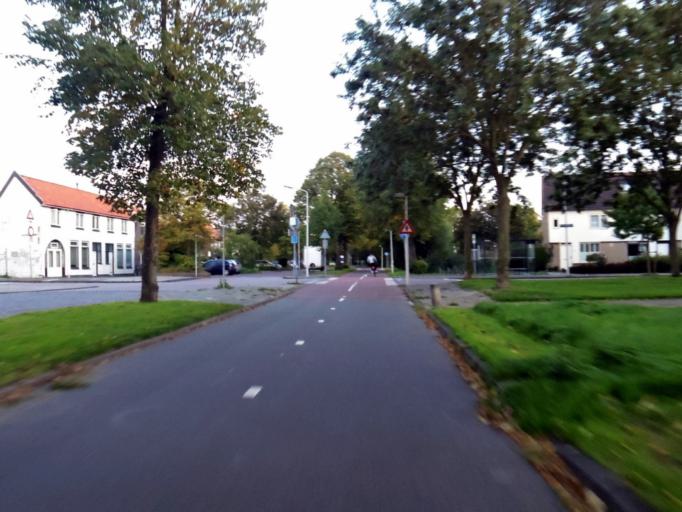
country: NL
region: South Holland
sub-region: Gemeente Oegstgeest
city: Oegstgeest
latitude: 52.1559
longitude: 4.4538
